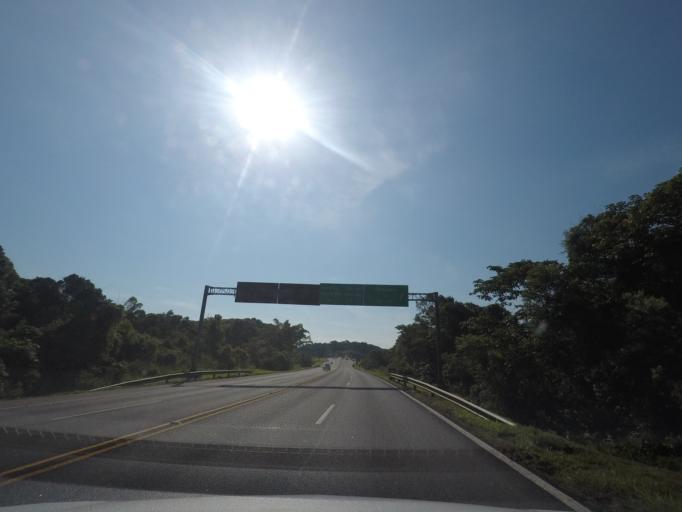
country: BR
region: Parana
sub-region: Paranagua
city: Paranagua
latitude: -25.5724
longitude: -48.6134
